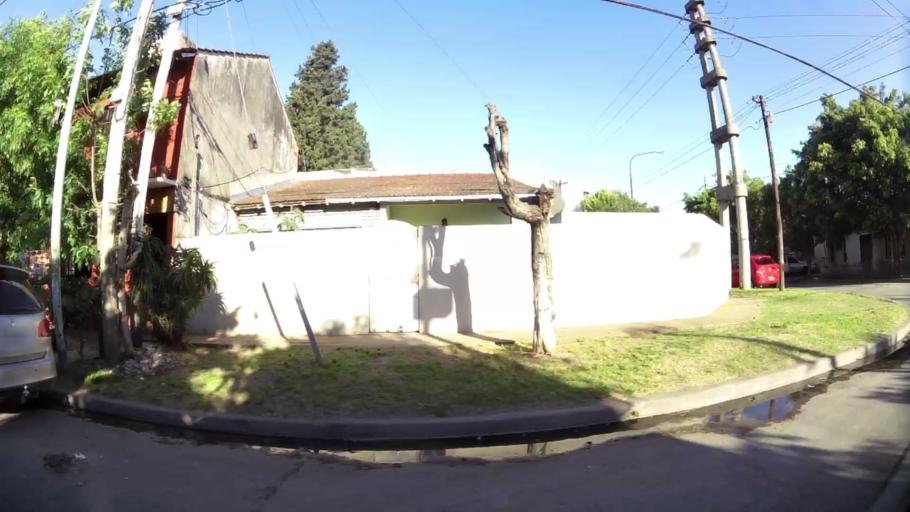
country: AR
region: Buenos Aires
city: Ituzaingo
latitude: -34.6889
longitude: -58.6397
